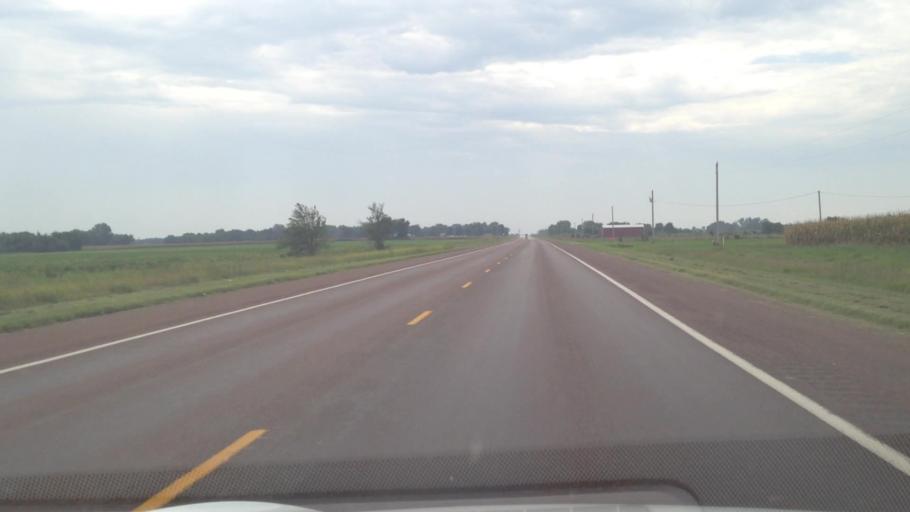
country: US
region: Kansas
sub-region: Crawford County
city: Girard
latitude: 37.4502
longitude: -94.8331
